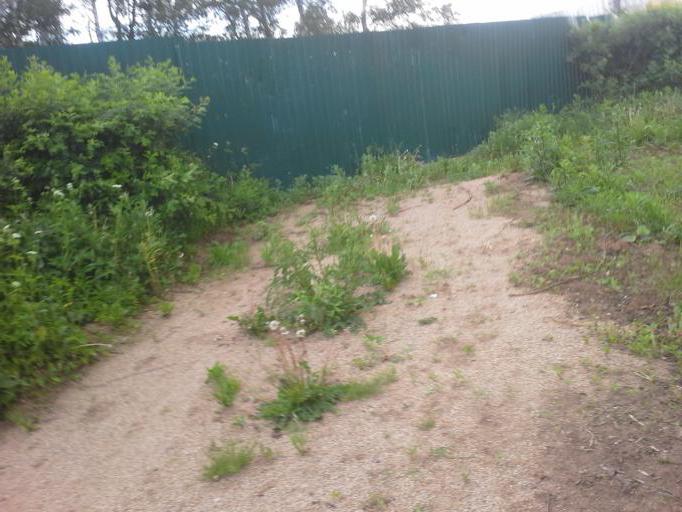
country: RU
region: Moskovskaya
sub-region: Leninskiy Rayon
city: Vnukovo
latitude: 55.6238
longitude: 37.2850
